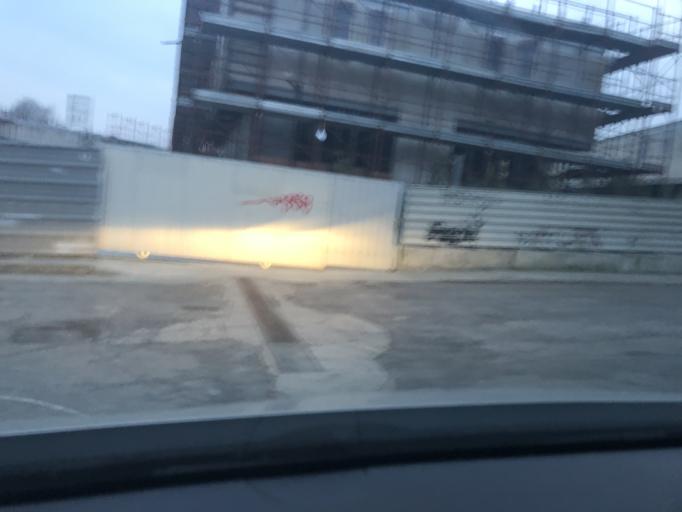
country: IT
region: Veneto
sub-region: Provincia di Verona
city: Sommacampagna
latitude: 45.4123
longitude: 10.8504
